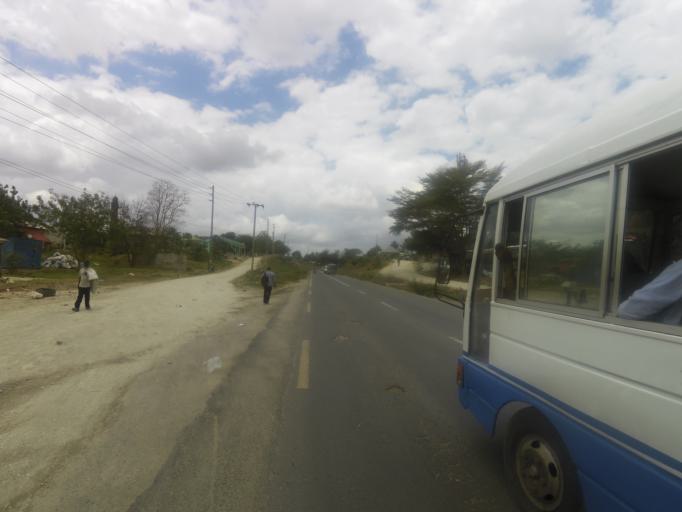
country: TZ
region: Pwani
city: Vikindu
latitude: -6.9390
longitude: 39.2767
